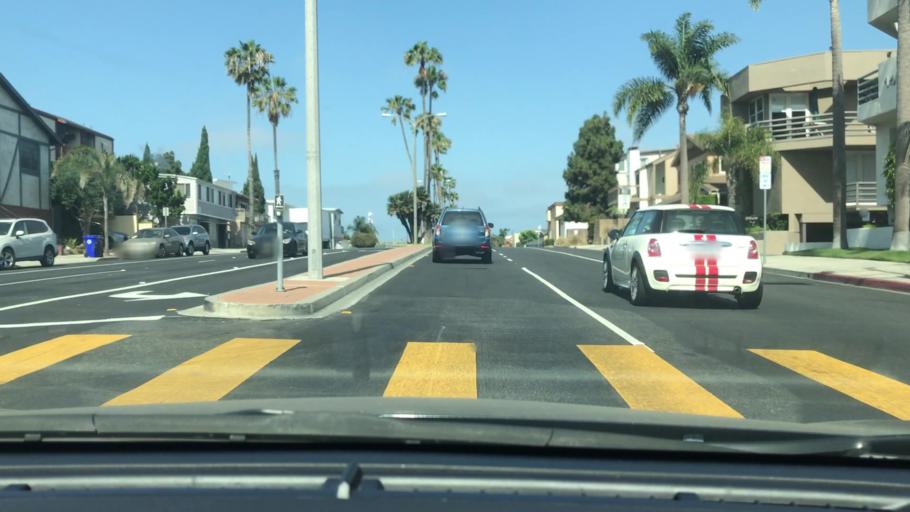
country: US
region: California
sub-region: Los Angeles County
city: Manhattan Beach
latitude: 33.8874
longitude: -118.3875
